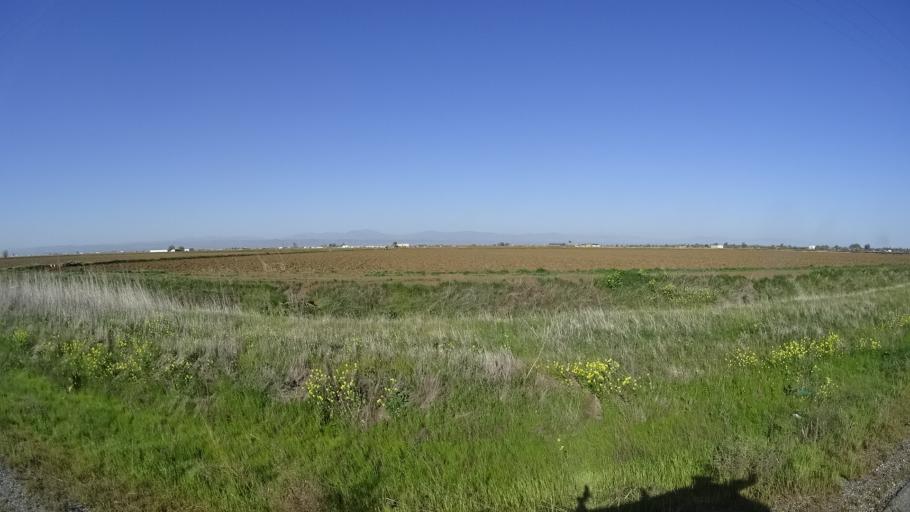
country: US
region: California
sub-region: Glenn County
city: Willows
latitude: 39.4991
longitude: -122.1745
